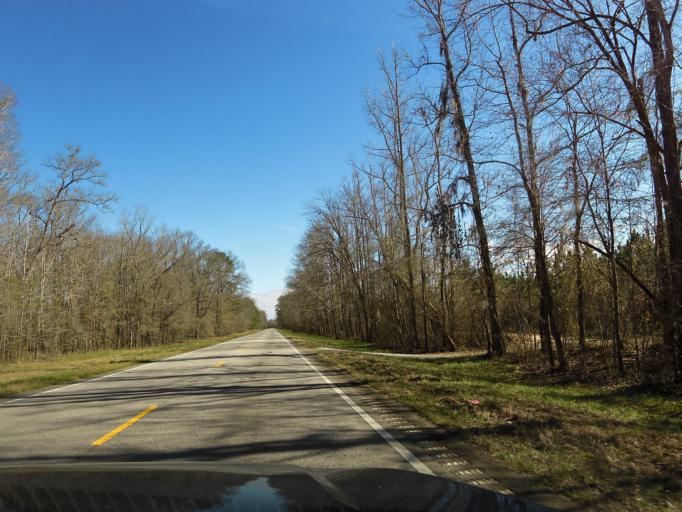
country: US
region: Alabama
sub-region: Barbour County
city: Clayton
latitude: 32.0494
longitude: -85.4368
